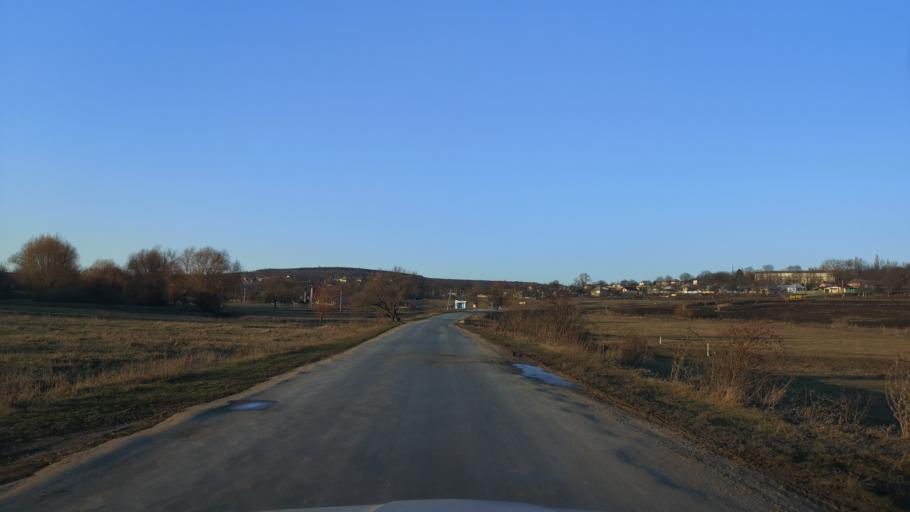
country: MD
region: Orhei
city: Orhei
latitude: 47.3513
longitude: 28.6954
